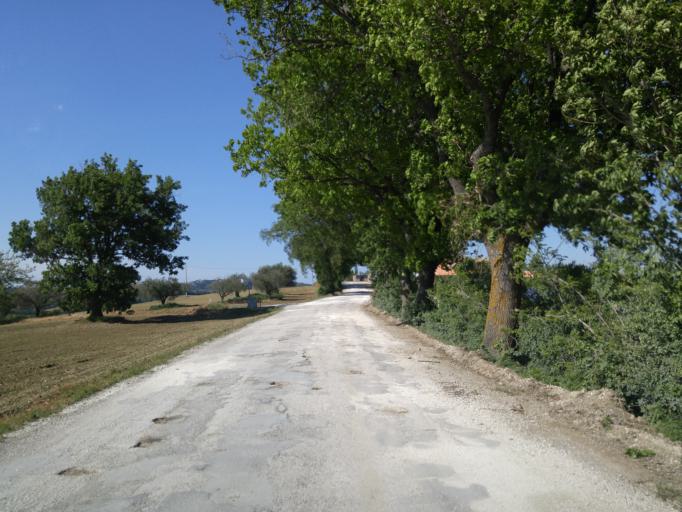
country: IT
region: The Marches
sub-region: Provincia di Pesaro e Urbino
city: Mombaroccio
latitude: 43.8064
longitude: 12.8877
